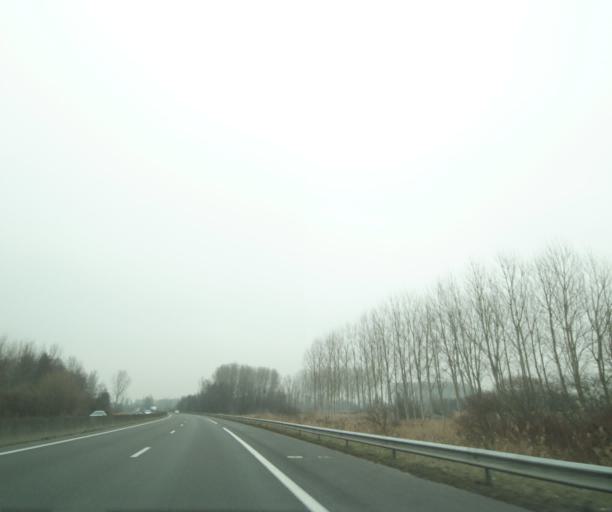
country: FR
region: Rhone-Alpes
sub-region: Departement du Rhone
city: Simandres
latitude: 45.6210
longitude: 4.8929
